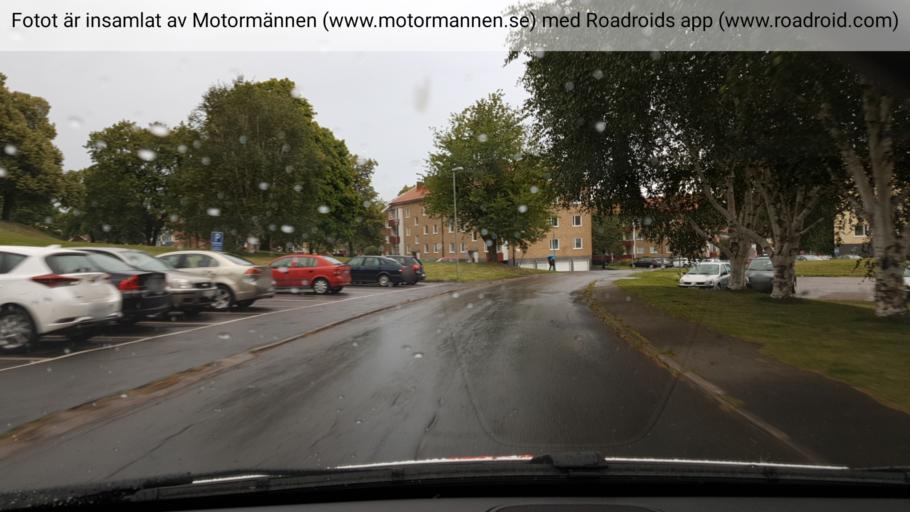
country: SE
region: Vaestra Goetaland
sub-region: Skovde Kommun
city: Skoevde
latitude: 58.3938
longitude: 13.8309
